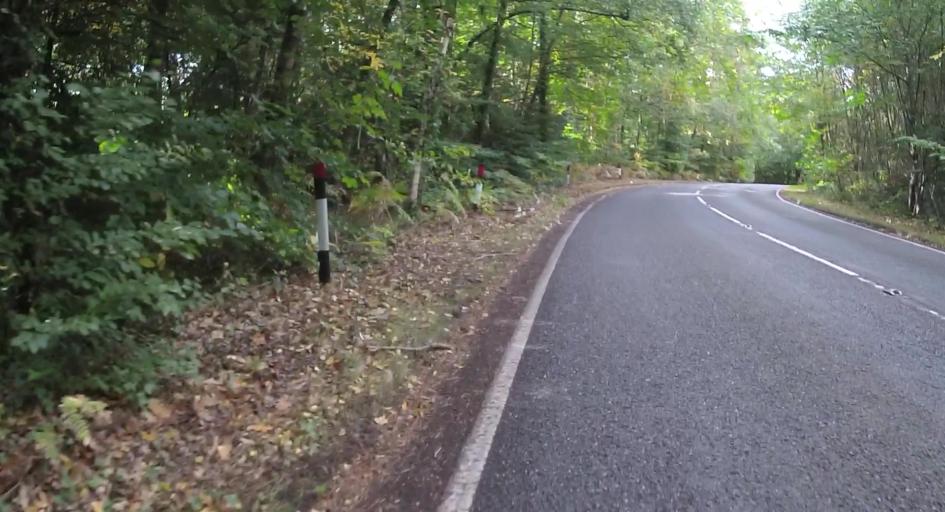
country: GB
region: England
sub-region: Surrey
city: Frimley
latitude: 51.2986
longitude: -0.7144
